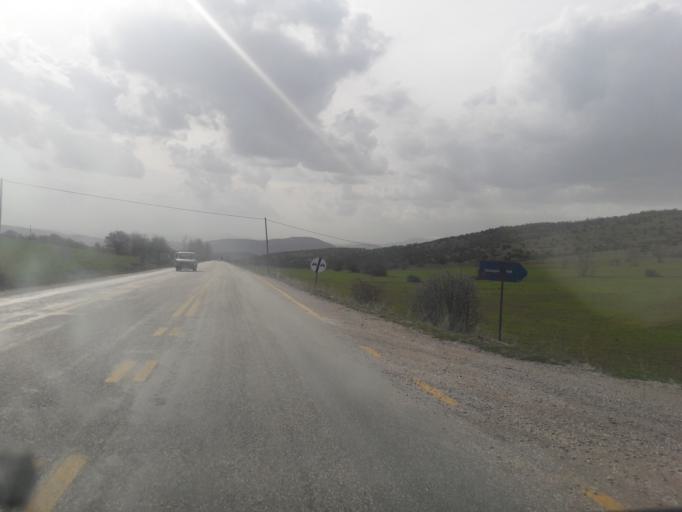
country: TR
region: Gumushane
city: Evren
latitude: 40.1690
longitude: 39.2738
